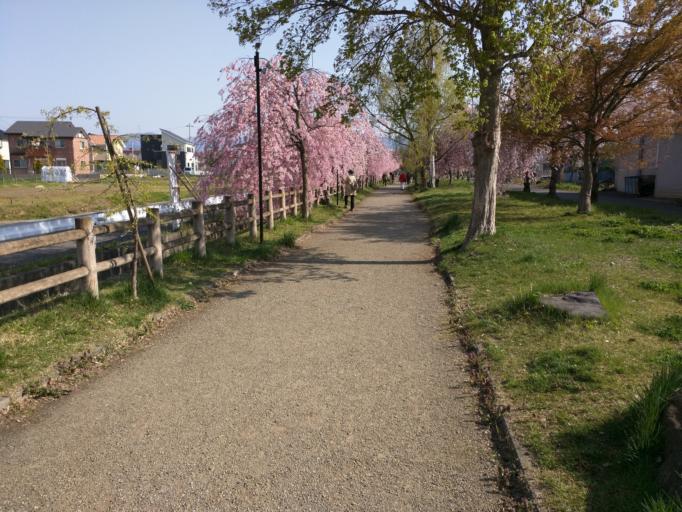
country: JP
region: Fukushima
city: Kitakata
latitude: 37.6578
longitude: 139.8676
